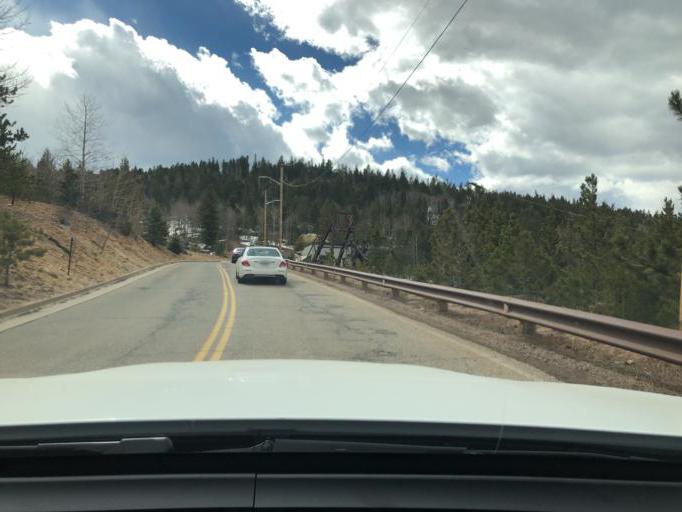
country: US
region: Colorado
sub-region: Gilpin County
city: Central City
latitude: 39.7950
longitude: -105.5122
